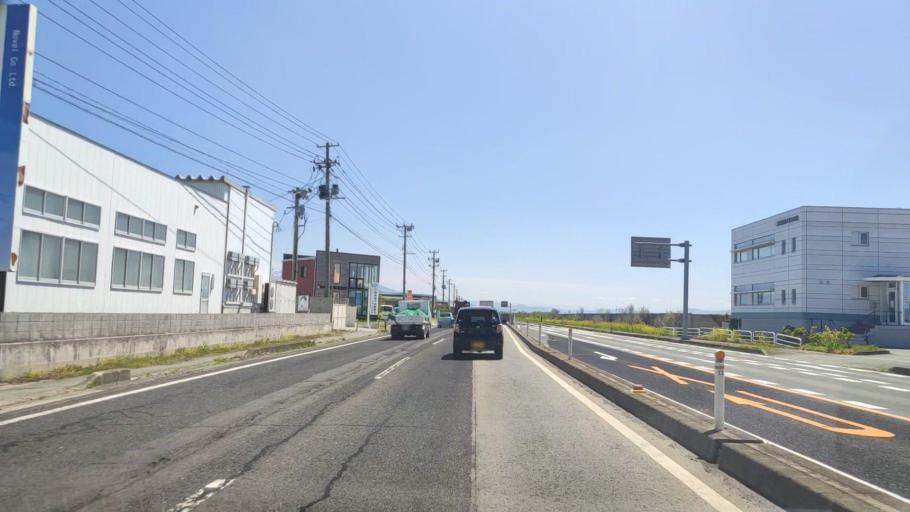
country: JP
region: Yamagata
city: Higashine
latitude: 38.4180
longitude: 140.3753
